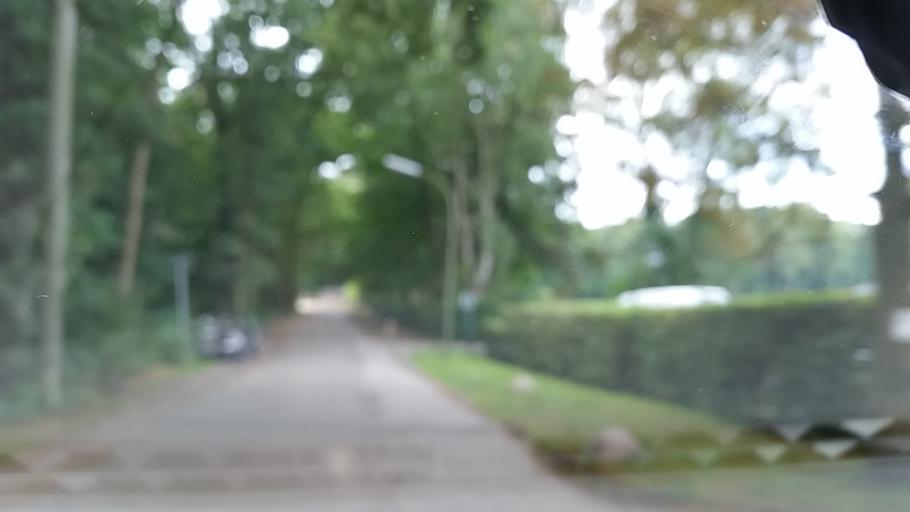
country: DE
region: Schleswig-Holstein
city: Wedel
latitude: 53.5720
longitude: 9.7744
